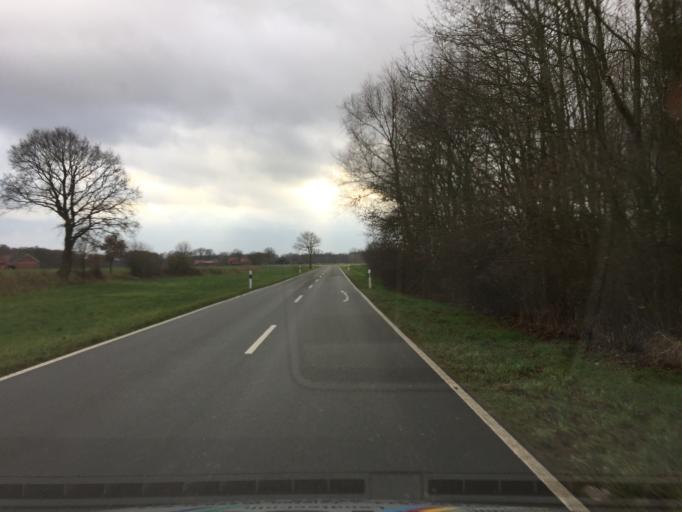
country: DE
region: Lower Saxony
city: Steyerberg
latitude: 52.5431
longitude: 9.0277
